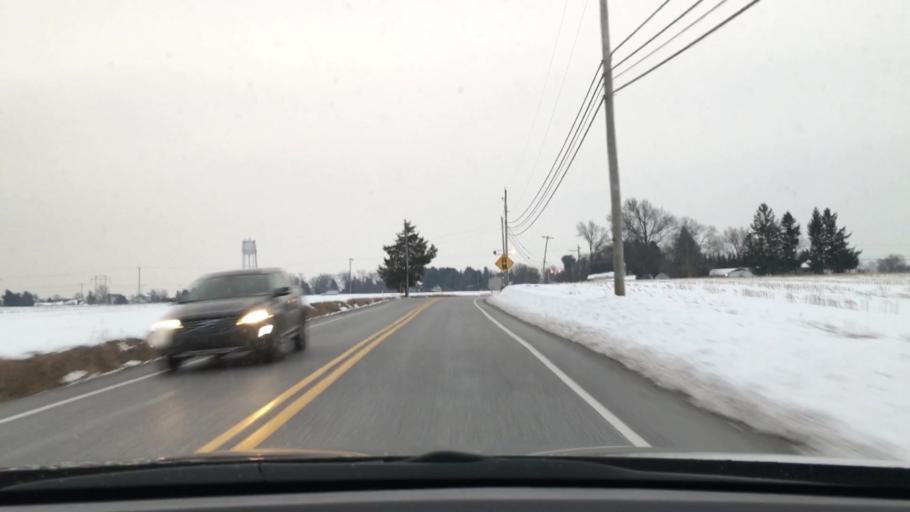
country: US
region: Pennsylvania
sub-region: York County
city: Dover
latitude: 39.9813
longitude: -76.8504
